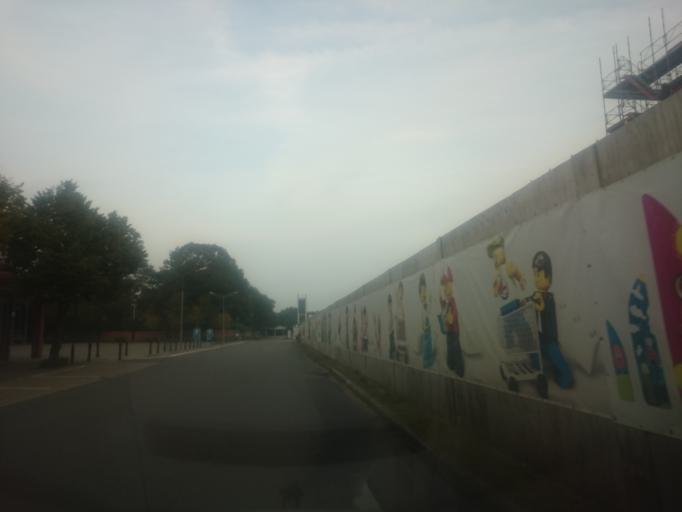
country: DK
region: South Denmark
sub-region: Billund Kommune
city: Billund
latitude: 55.7312
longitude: 9.1147
